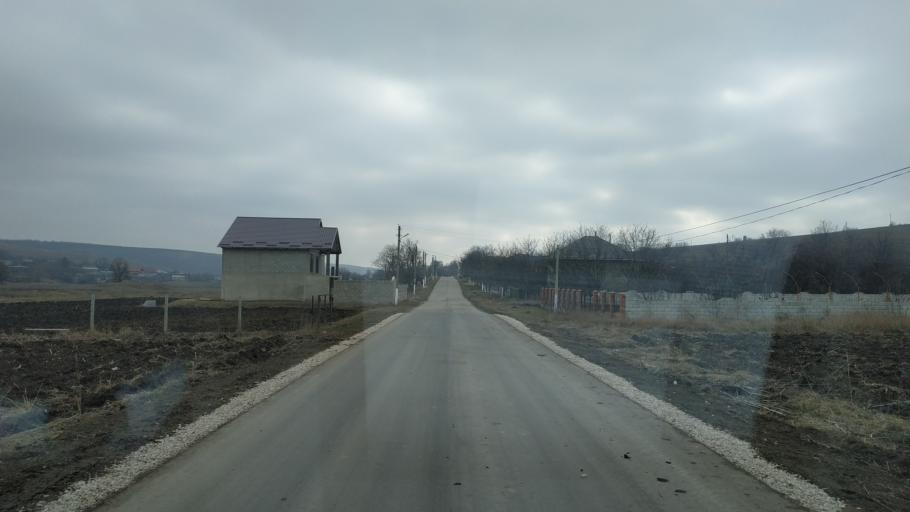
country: MD
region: Hincesti
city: Dancu
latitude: 46.8931
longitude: 28.3243
